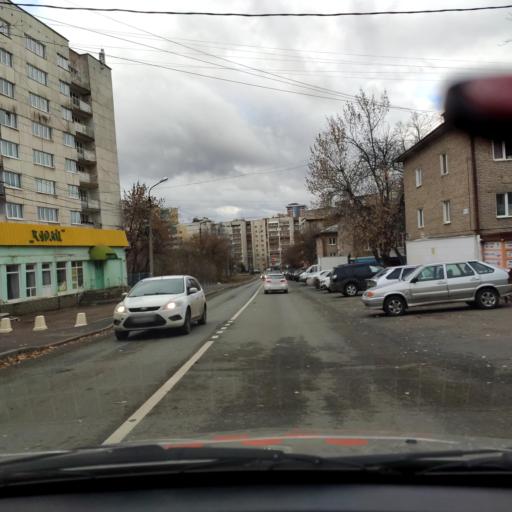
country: RU
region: Bashkortostan
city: Ufa
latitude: 54.7170
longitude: 55.9991
